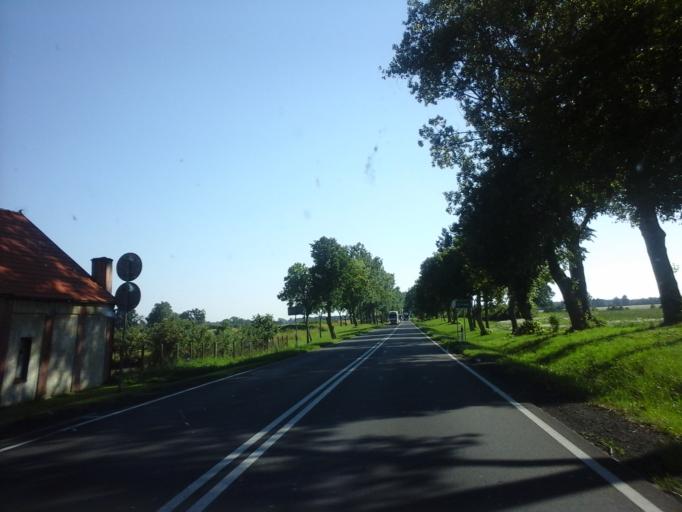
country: PL
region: West Pomeranian Voivodeship
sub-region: Powiat gryficki
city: Ploty
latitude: 53.7712
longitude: 15.2428
